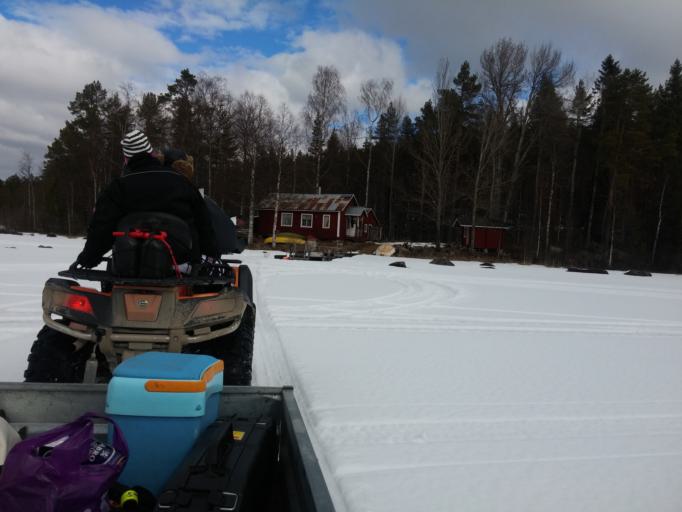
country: SE
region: Gaevleborg
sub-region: Ljusdals Kommun
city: Farila
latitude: 62.1648
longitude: 15.8209
